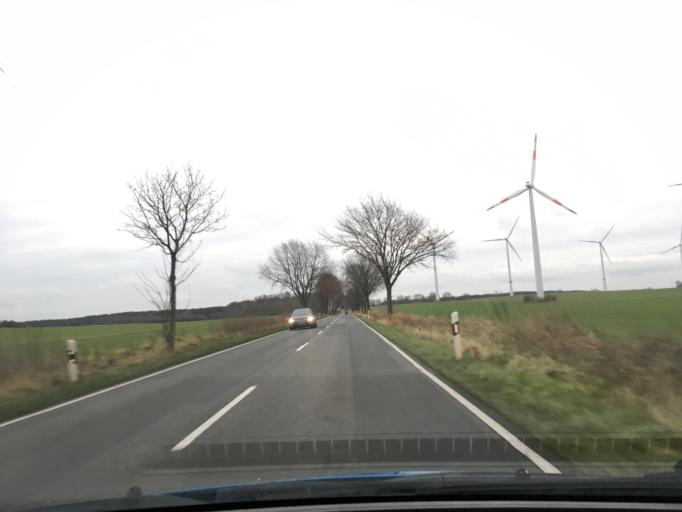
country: DE
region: Lower Saxony
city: Reinstorf
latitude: 53.2646
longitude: 10.5680
